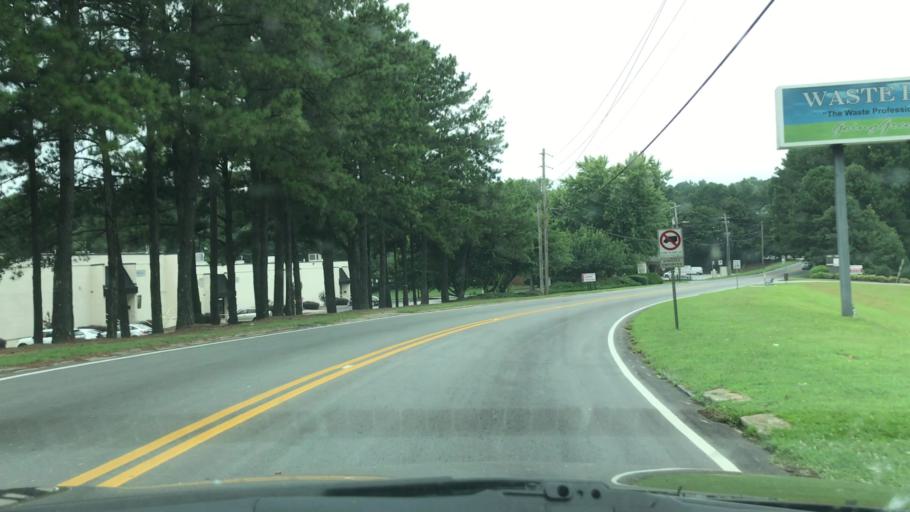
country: US
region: Georgia
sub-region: DeKalb County
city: Doraville
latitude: 33.9019
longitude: -84.2525
